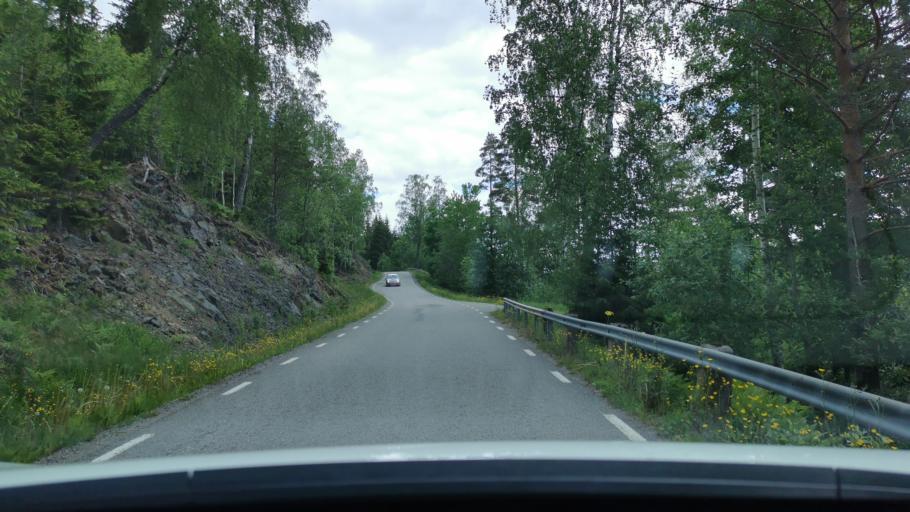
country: SE
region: Vaestra Goetaland
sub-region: Bengtsfors Kommun
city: Dals Langed
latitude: 58.8286
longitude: 12.3306
